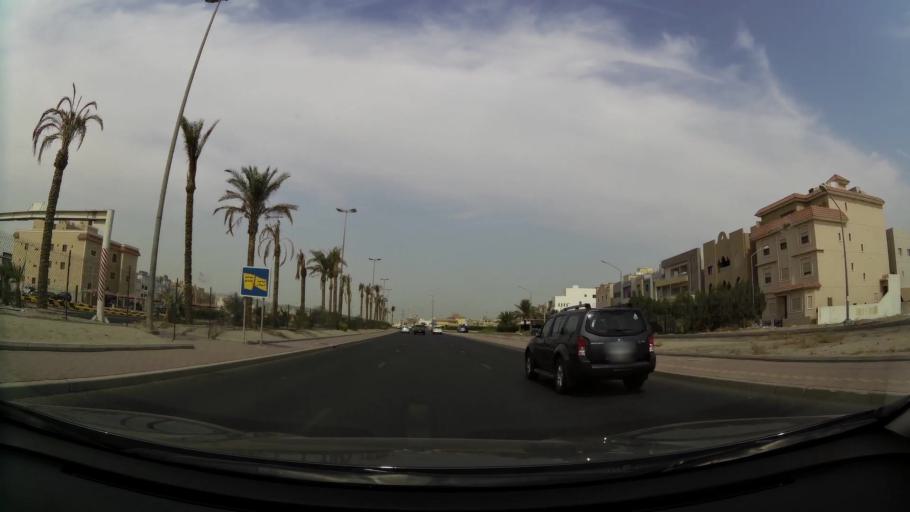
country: KW
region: Al Farwaniyah
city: Janub as Surrah
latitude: 29.2945
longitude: 48.0029
